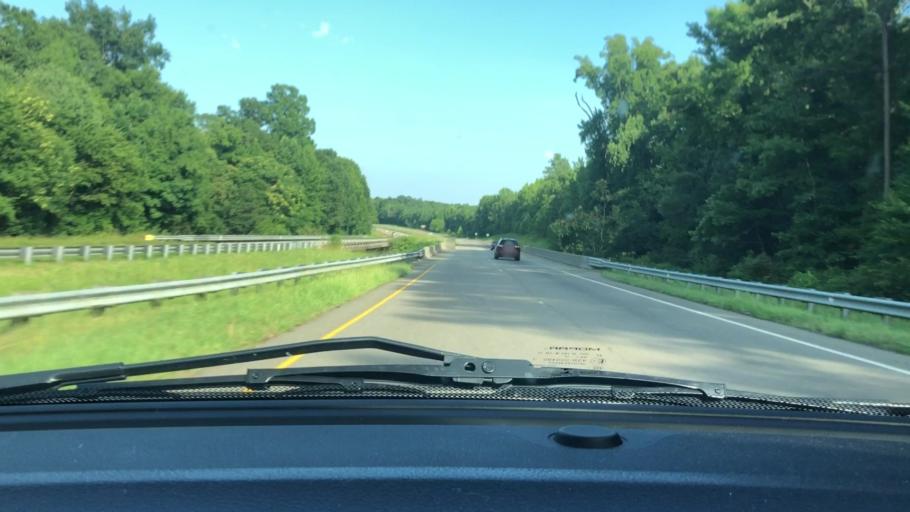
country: US
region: North Carolina
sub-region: Chatham County
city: Farmville
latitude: 35.6130
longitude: -79.3448
